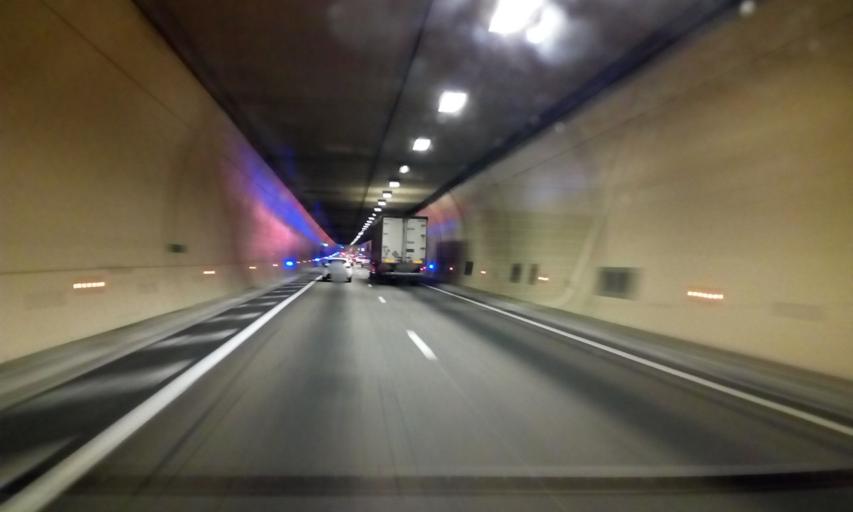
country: FR
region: Provence-Alpes-Cote d'Azur
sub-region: Departement du Var
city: Toulon
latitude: 43.1246
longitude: 5.9296
